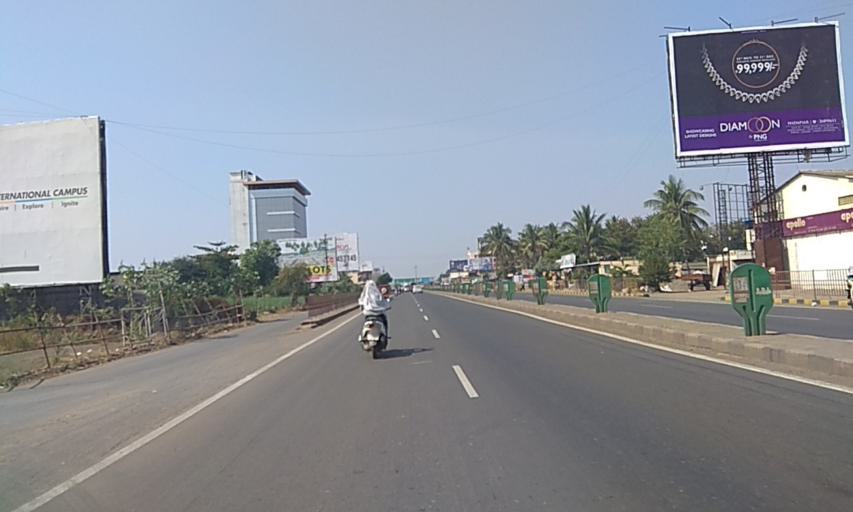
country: IN
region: Maharashtra
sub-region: Pune Division
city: Lohogaon
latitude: 18.4925
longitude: 73.9973
